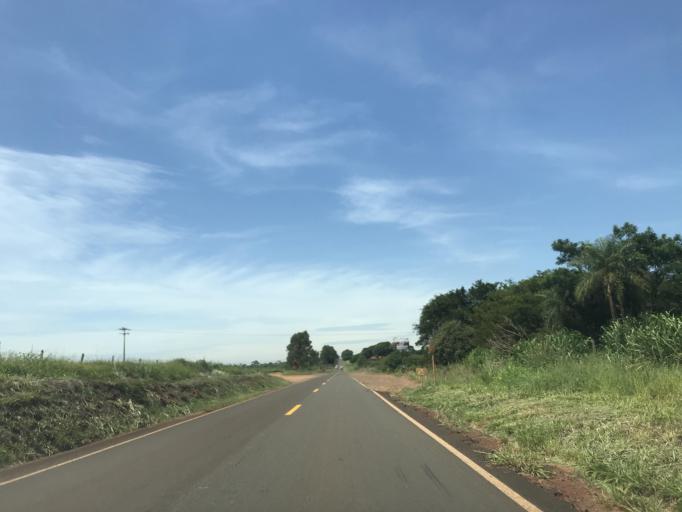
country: BR
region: Parana
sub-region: Paranavai
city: Nova Aurora
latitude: -22.8191
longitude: -52.6550
